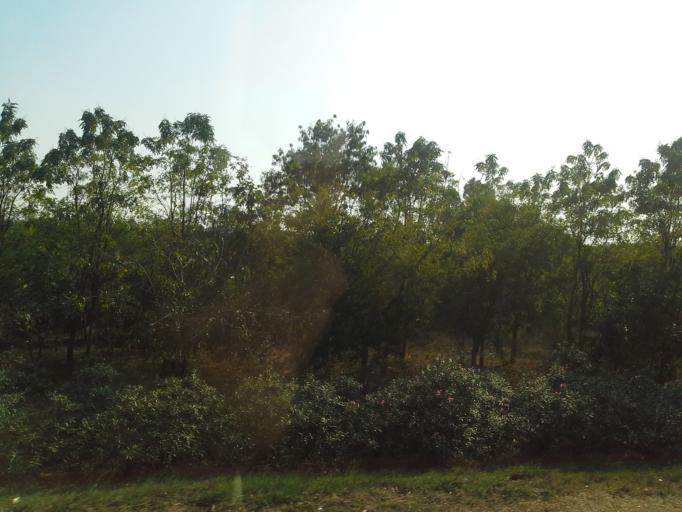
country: IN
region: Telangana
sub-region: Rangareddi
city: Balapur
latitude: 17.2407
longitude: 78.4234
